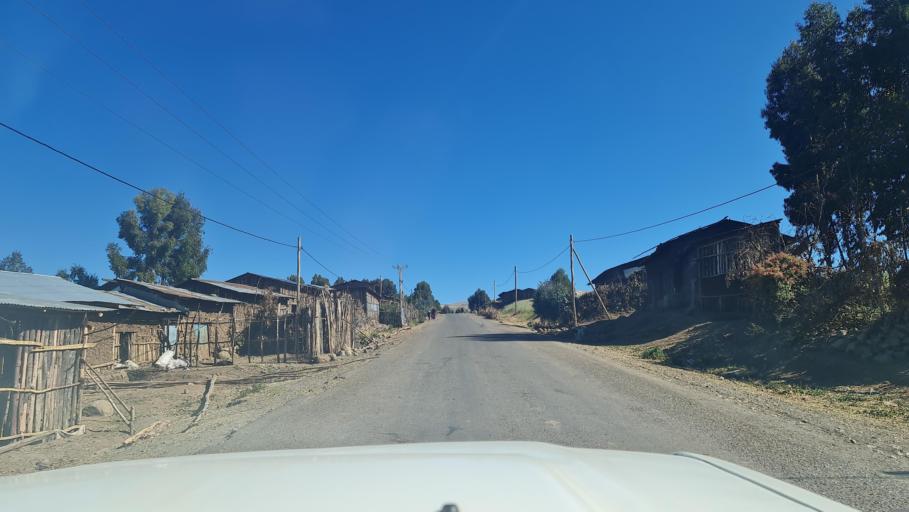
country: ET
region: Amhara
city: Debark'
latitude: 13.1022
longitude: 38.1440
